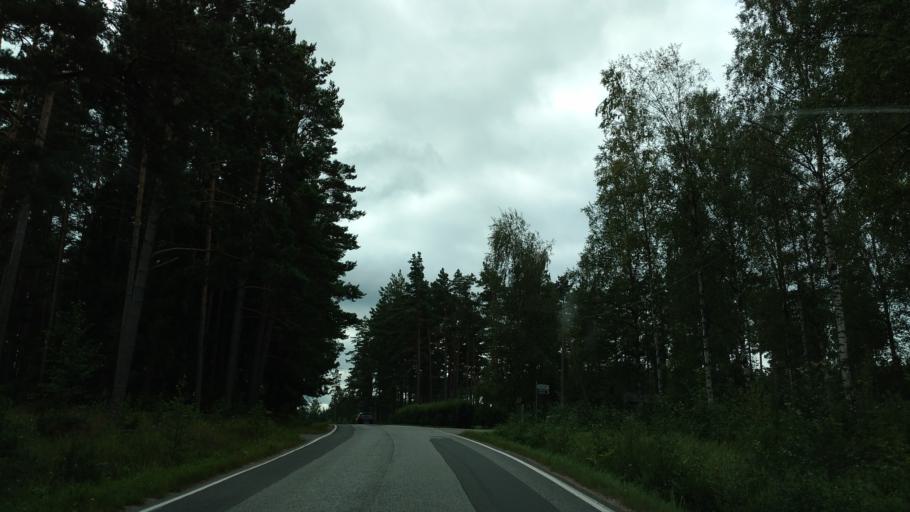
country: FI
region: Varsinais-Suomi
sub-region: Aboland-Turunmaa
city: Dragsfjaerd
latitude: 60.0686
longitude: 22.4503
